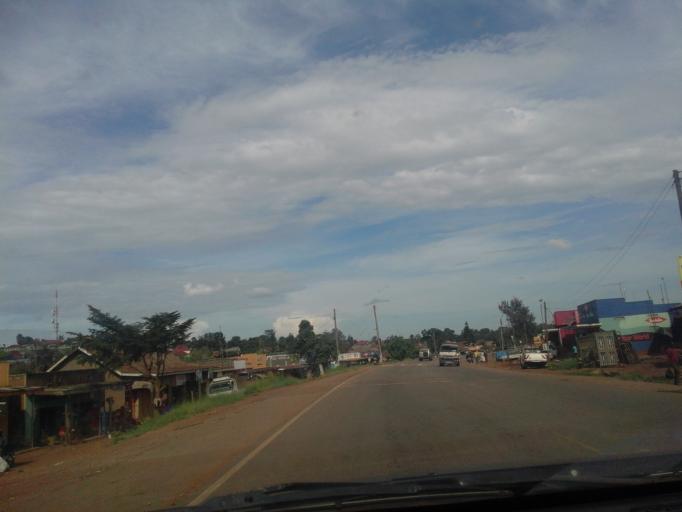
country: UG
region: Central Region
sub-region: Lwengo District
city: Lwengo
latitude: -0.3535
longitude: 31.5506
